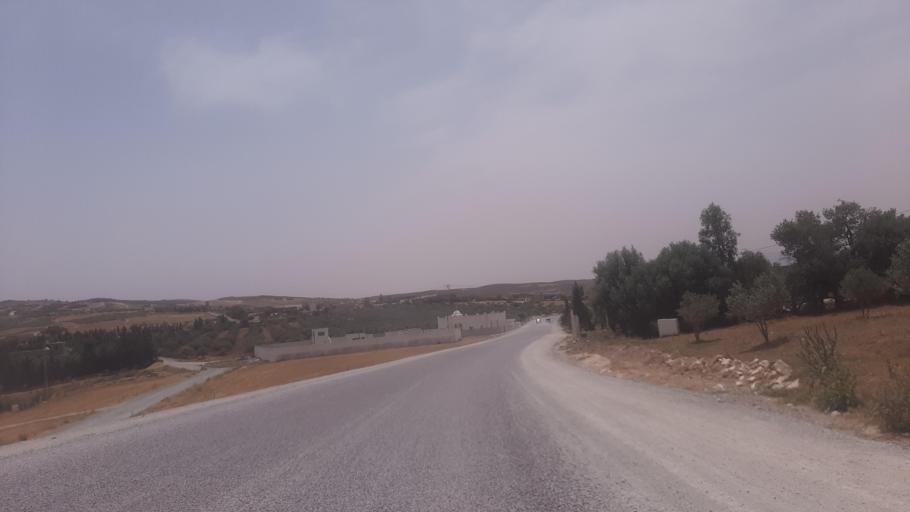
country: TN
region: Zaghwan
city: Zaghouan
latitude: 36.5296
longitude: 10.1586
